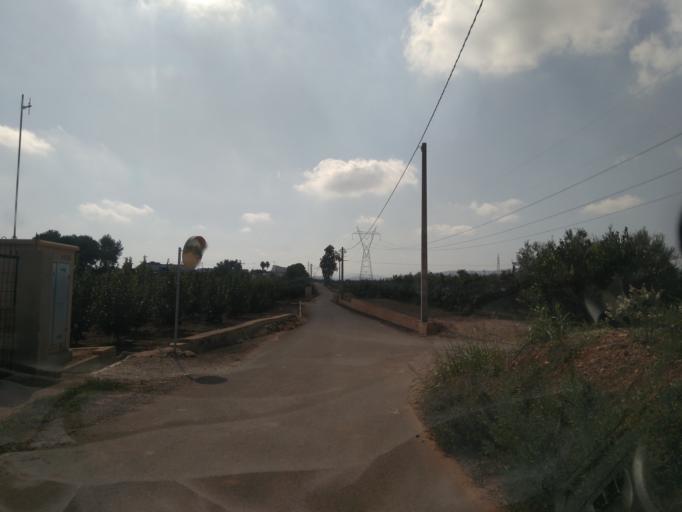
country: ES
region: Valencia
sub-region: Provincia de Valencia
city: Masalaves
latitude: 39.1763
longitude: -0.5515
